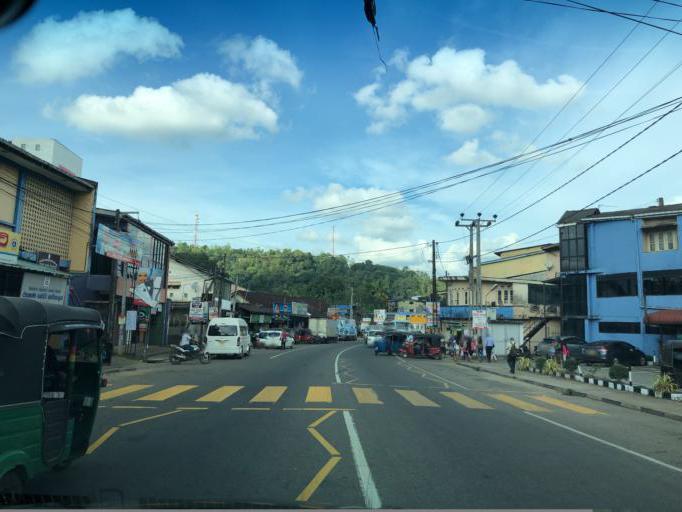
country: LK
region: Western
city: Horawala Junction
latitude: 6.5225
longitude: 80.1120
